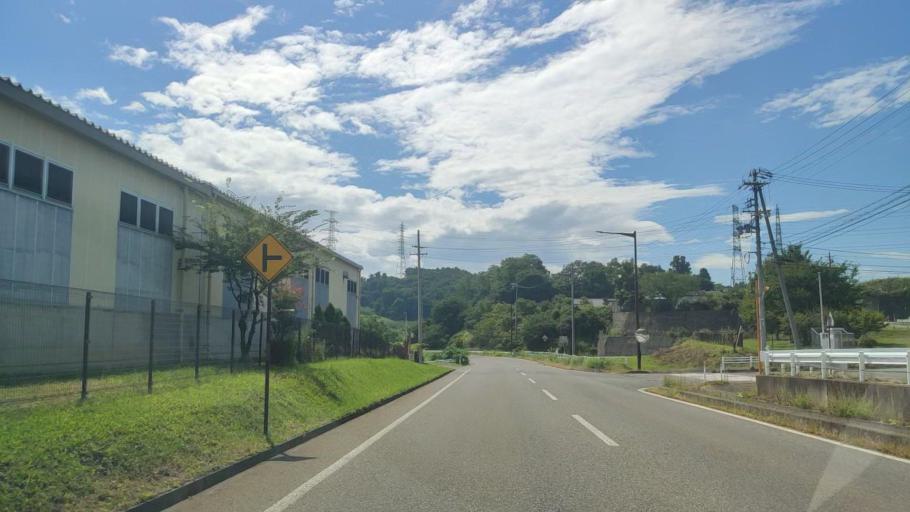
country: JP
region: Nagano
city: Nakano
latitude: 36.7386
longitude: 138.3051
